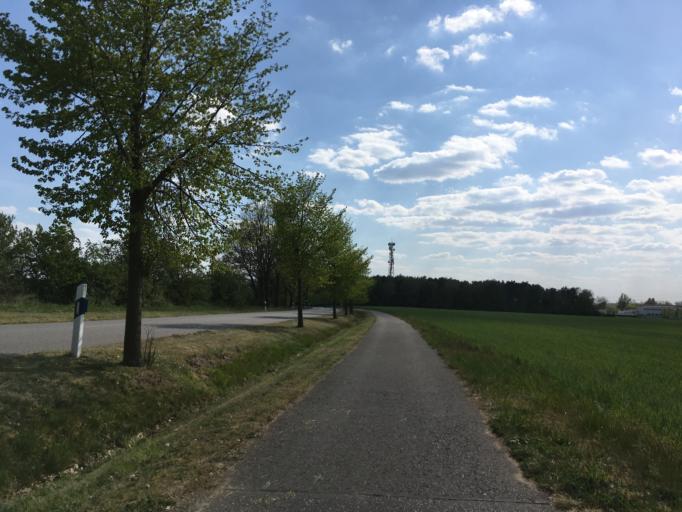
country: DE
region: Brandenburg
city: Ahrensfelde
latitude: 52.5933
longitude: 13.5656
